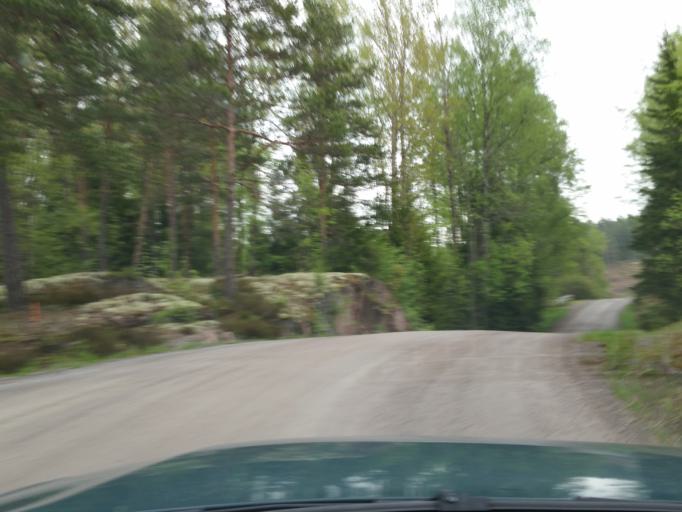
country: FI
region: Uusimaa
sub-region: Helsinki
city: Karjalohja
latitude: 60.1830
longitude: 23.6782
